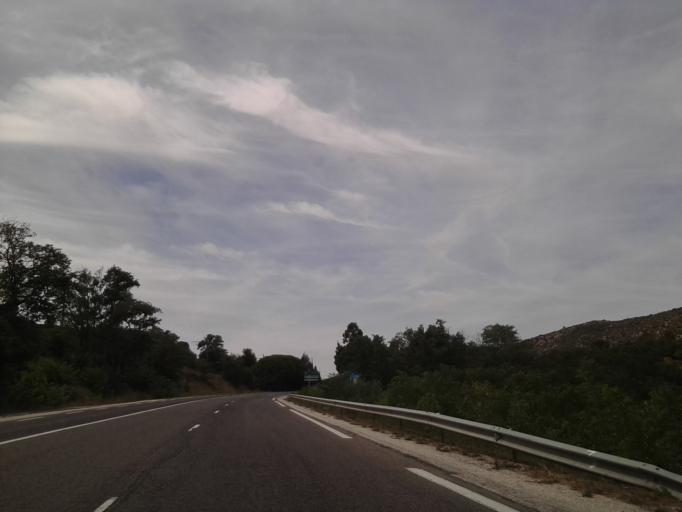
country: FR
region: Languedoc-Roussillon
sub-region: Departement des Pyrenees-Orientales
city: Vinca
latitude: 42.6523
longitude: 2.5501
